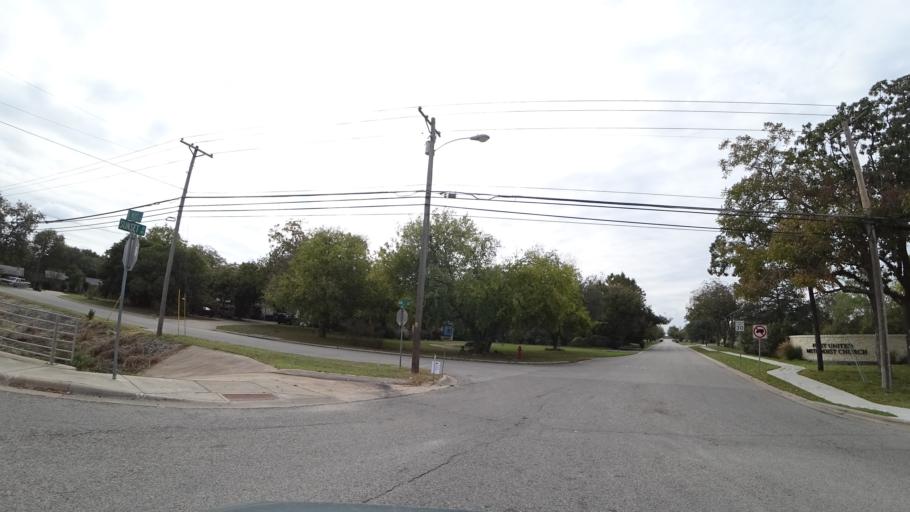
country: US
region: Texas
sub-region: Williamson County
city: Round Rock
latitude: 30.5149
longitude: -97.6817
